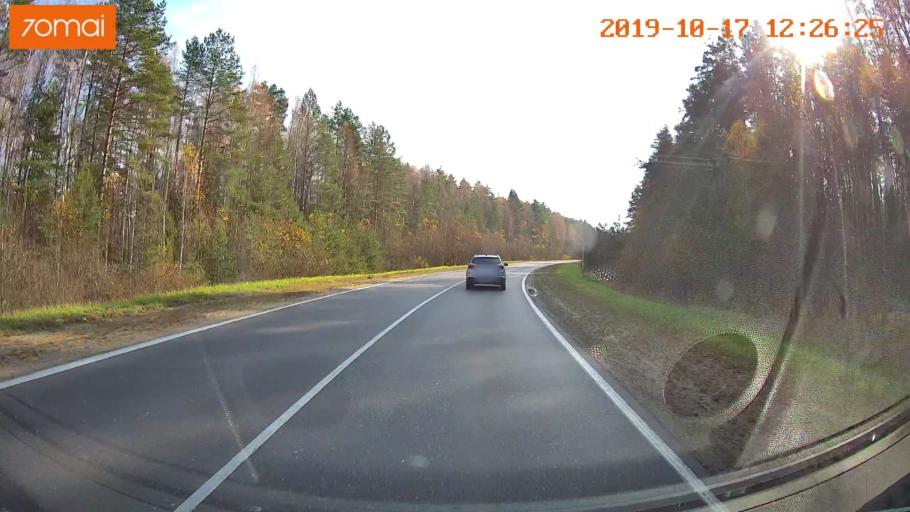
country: RU
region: Rjazan
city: Syntul
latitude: 55.0195
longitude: 41.2557
